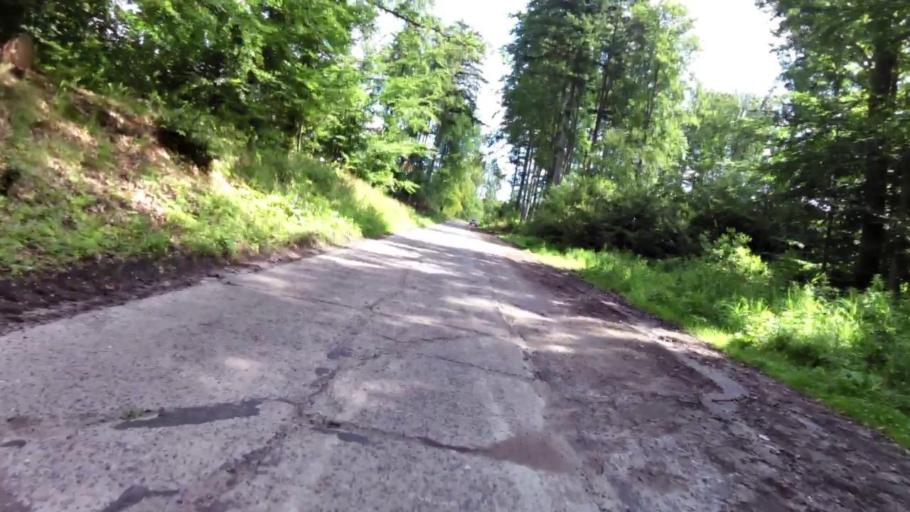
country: PL
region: West Pomeranian Voivodeship
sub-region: Powiat stargardzki
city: Insko
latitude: 53.3963
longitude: 15.5081
